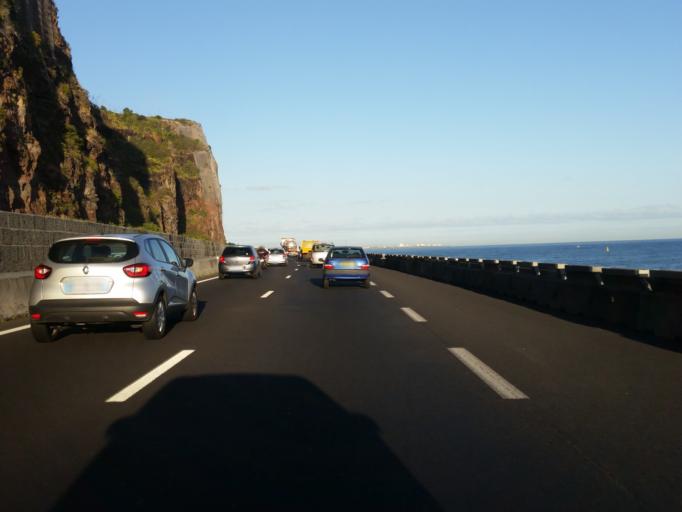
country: RE
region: Reunion
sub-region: Reunion
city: La Possession
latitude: -20.9097
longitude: 55.3567
